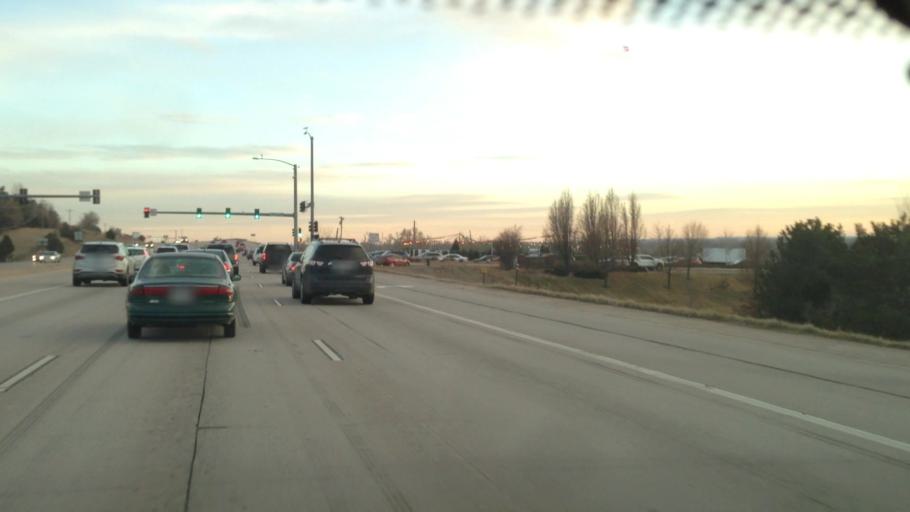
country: US
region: Colorado
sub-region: Arapahoe County
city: Dove Valley
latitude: 39.5797
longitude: -104.7933
